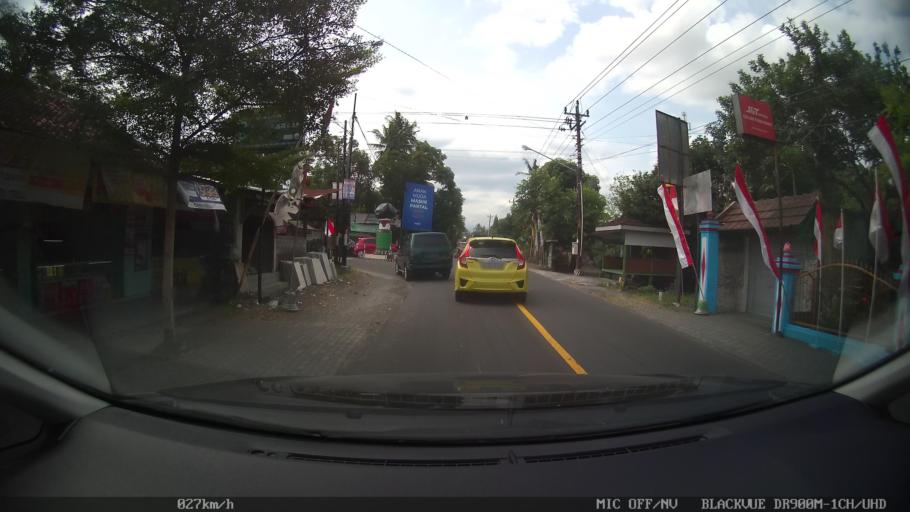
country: ID
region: Central Java
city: Candi Prambanan
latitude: -7.7290
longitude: 110.4721
